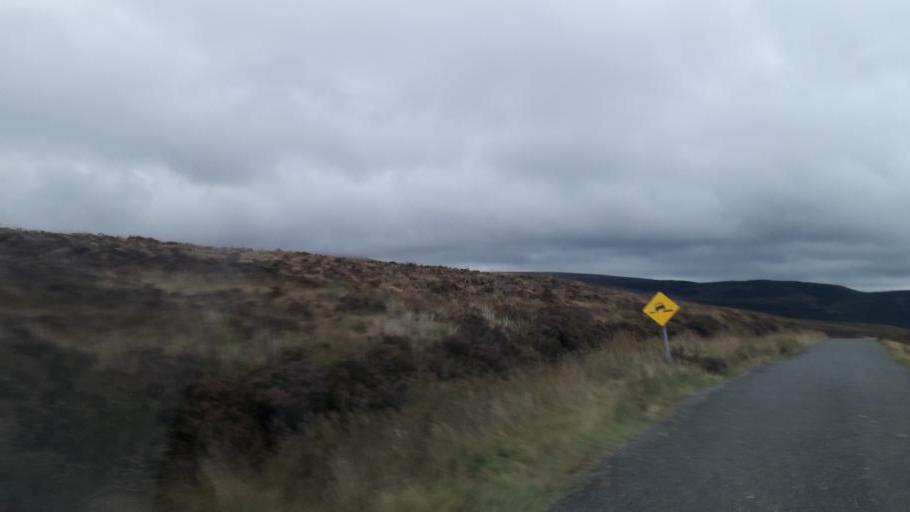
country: IE
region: Leinster
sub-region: Wicklow
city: Enniskerry
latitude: 53.1316
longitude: -6.2984
